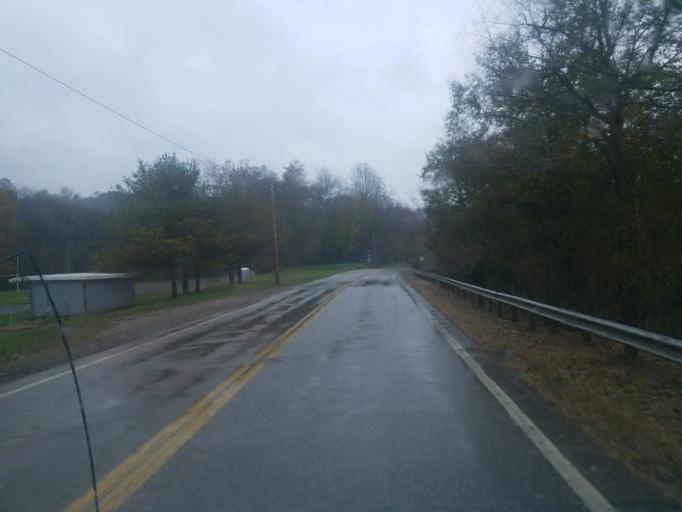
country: US
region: Ohio
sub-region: Morgan County
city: McConnelsville
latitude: 39.6107
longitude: -81.8175
